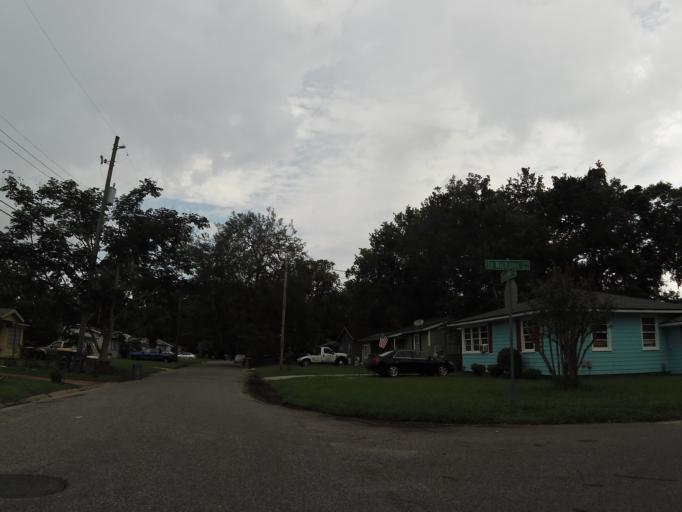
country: US
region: Florida
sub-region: Duval County
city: Jacksonville
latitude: 30.2973
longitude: -81.6349
